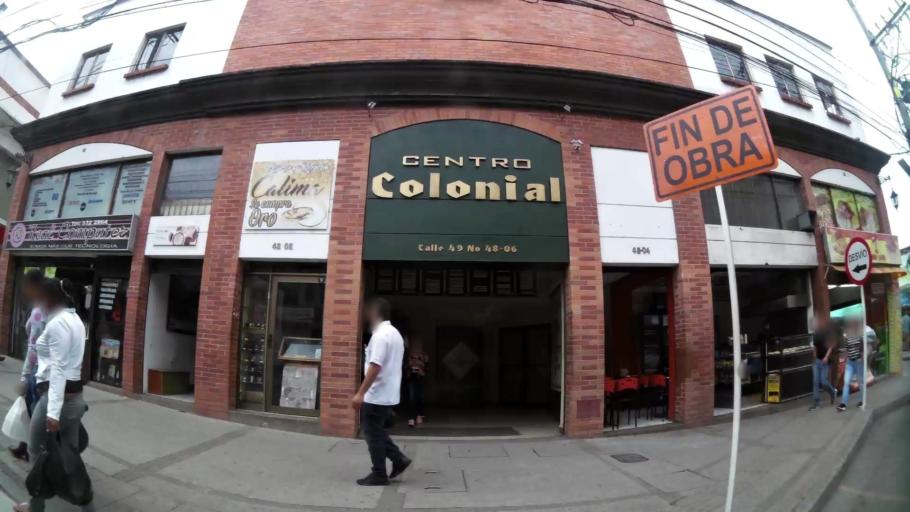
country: CO
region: Antioquia
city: Rionegro
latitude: 6.1532
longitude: -75.3725
